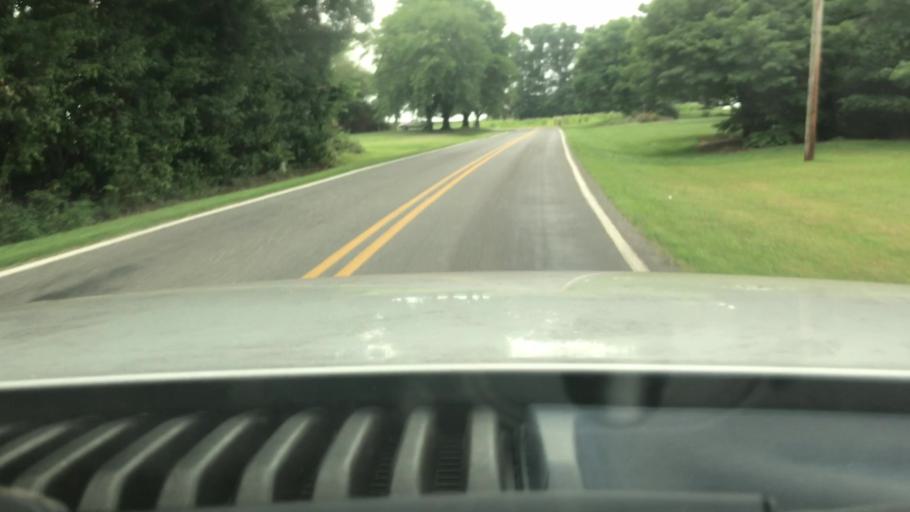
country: US
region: North Carolina
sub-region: Surry County
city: Dobson
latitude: 36.4030
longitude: -80.8044
